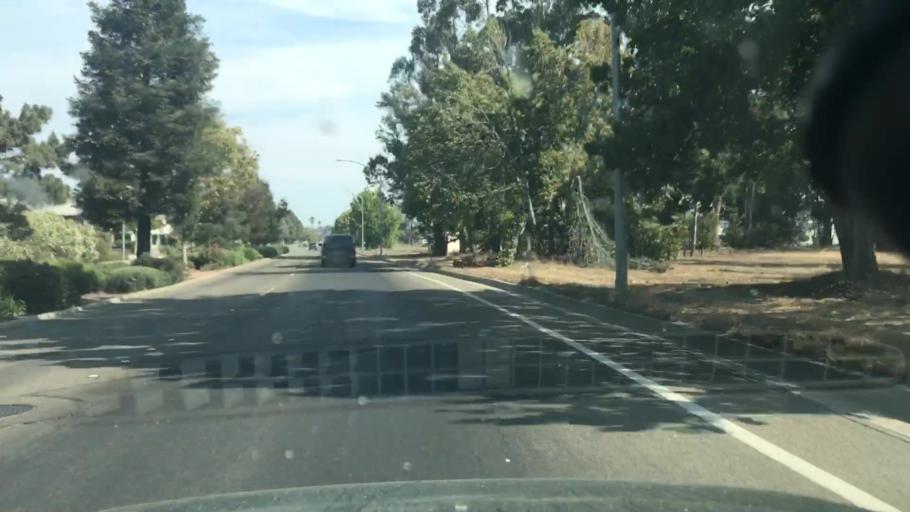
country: US
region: California
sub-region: Santa Barbara County
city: Orcutt
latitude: 34.9062
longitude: -120.4534
